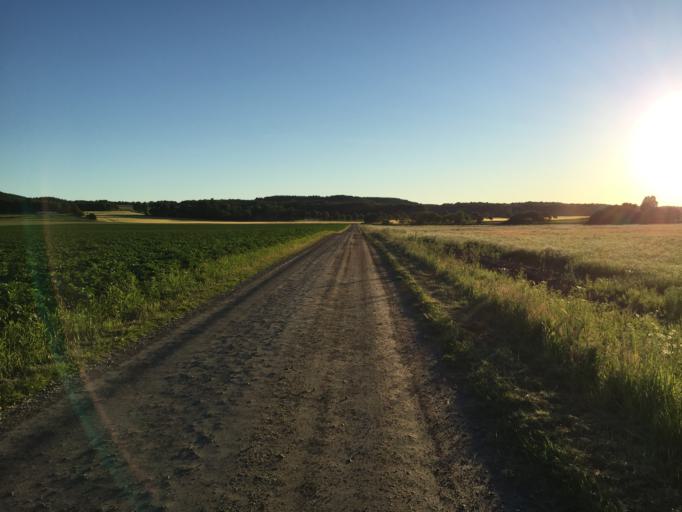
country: SE
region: Skane
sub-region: Lunds Kommun
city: Veberod
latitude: 55.6328
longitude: 13.4841
